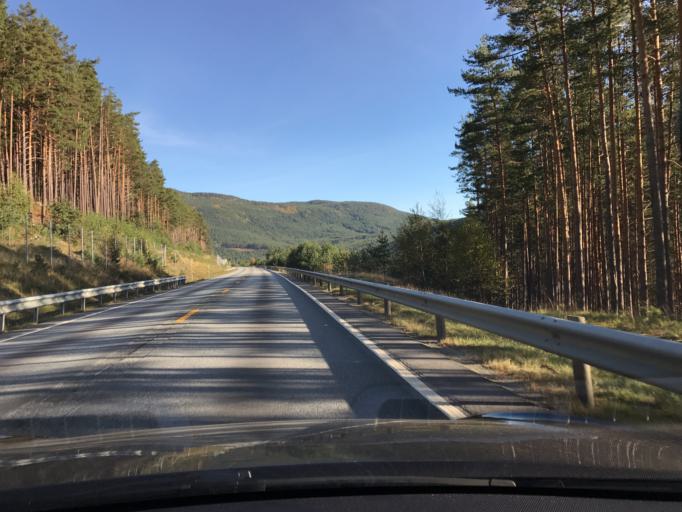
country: NO
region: Sogn og Fjordane
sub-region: Sogndal
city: Sogndalsfjora
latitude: 61.1836
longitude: 7.2642
